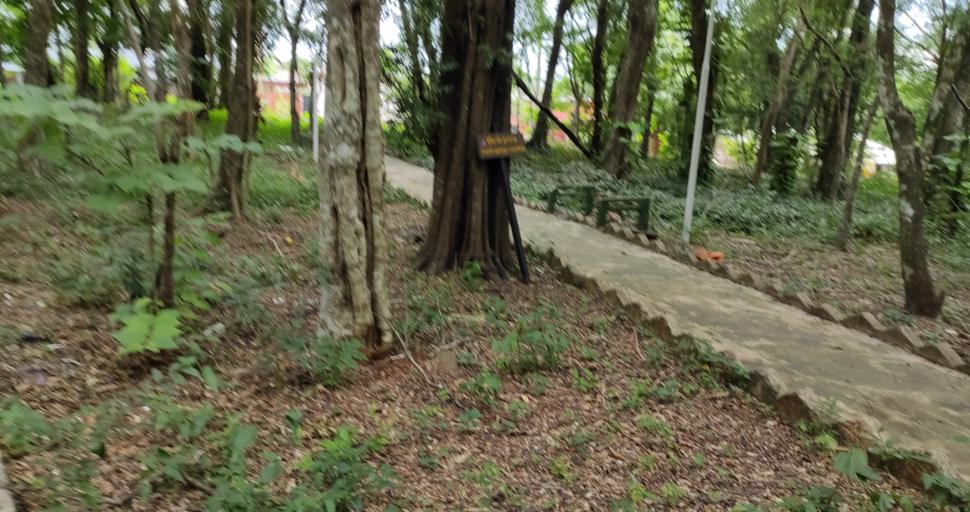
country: AR
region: Misiones
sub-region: Departamento de Iguazu
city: Puerto Iguazu
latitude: -25.5948
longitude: -54.5753
